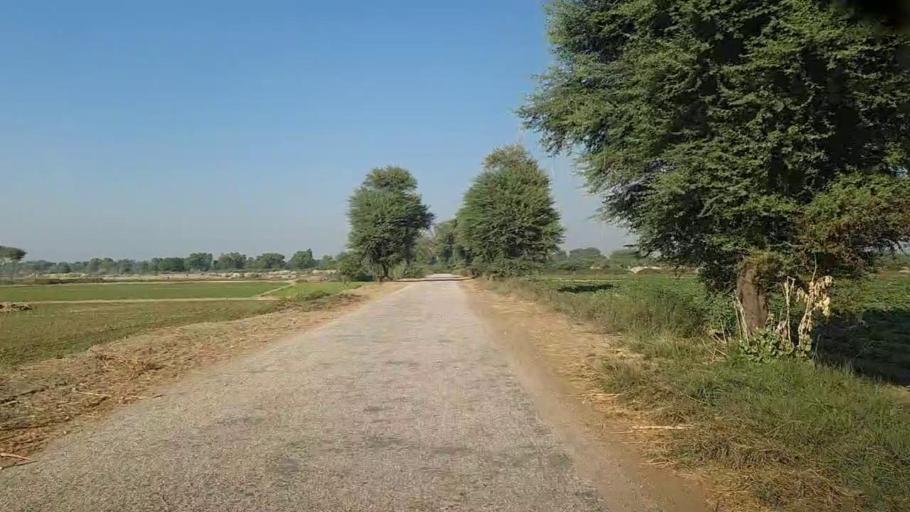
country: PK
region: Sindh
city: Darya Khan Marri
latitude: 26.6877
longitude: 68.3514
